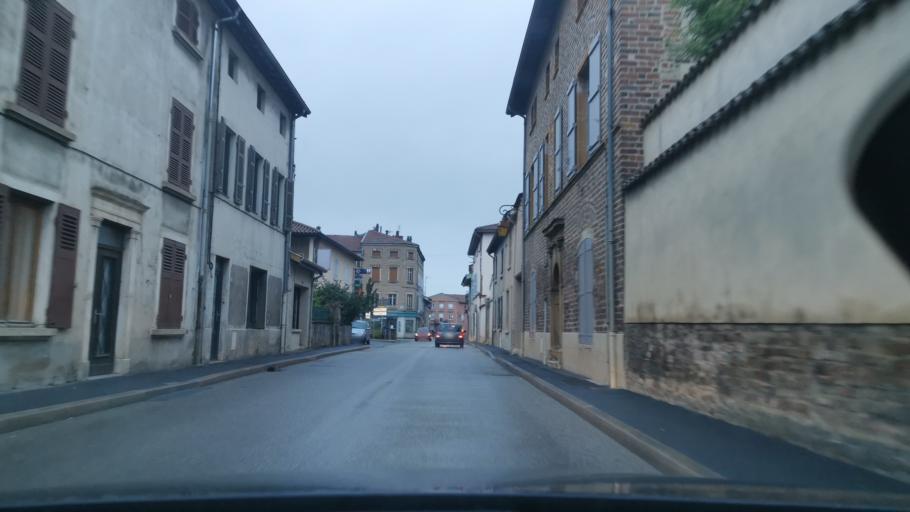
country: FR
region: Rhone-Alpes
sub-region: Departement de l'Ain
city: Saint-Trivier-sur-Moignans
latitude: 46.0712
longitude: 4.8980
